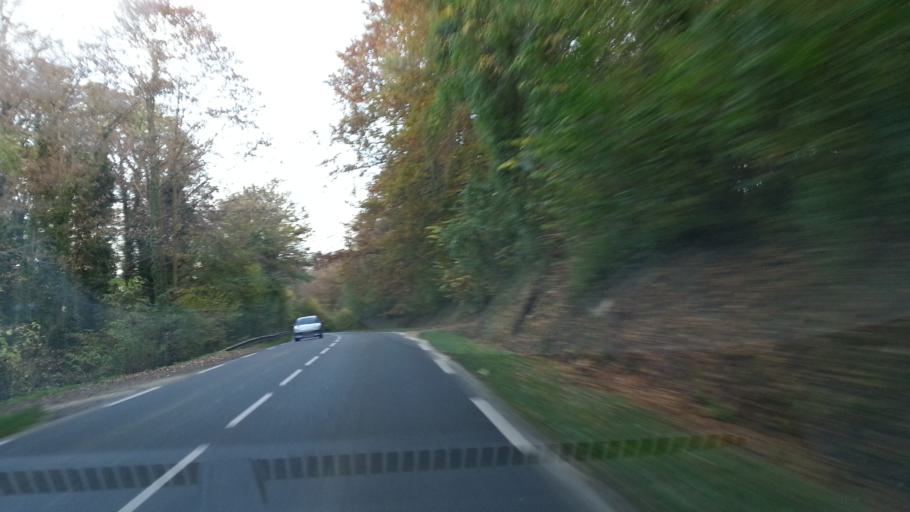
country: FR
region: Picardie
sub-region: Departement de l'Oise
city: Cires-les-Mello
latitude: 49.2856
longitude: 2.3592
